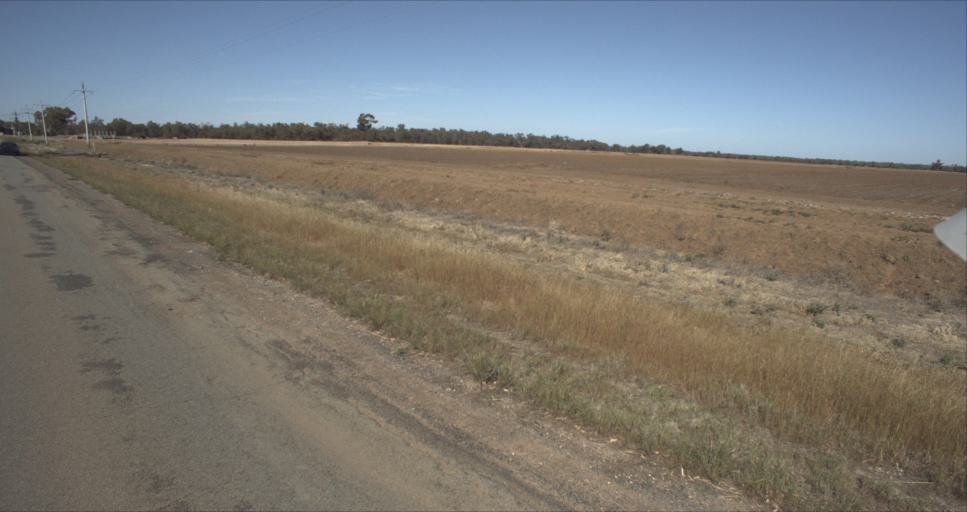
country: AU
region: New South Wales
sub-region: Leeton
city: Leeton
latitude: -34.6027
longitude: 146.2574
